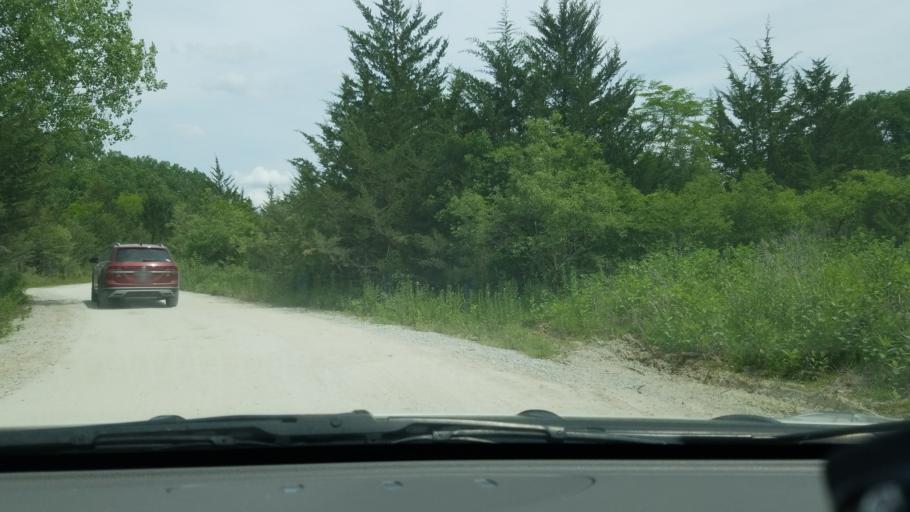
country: US
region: Nebraska
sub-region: Saunders County
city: Ashland
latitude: 41.0146
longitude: -96.2944
